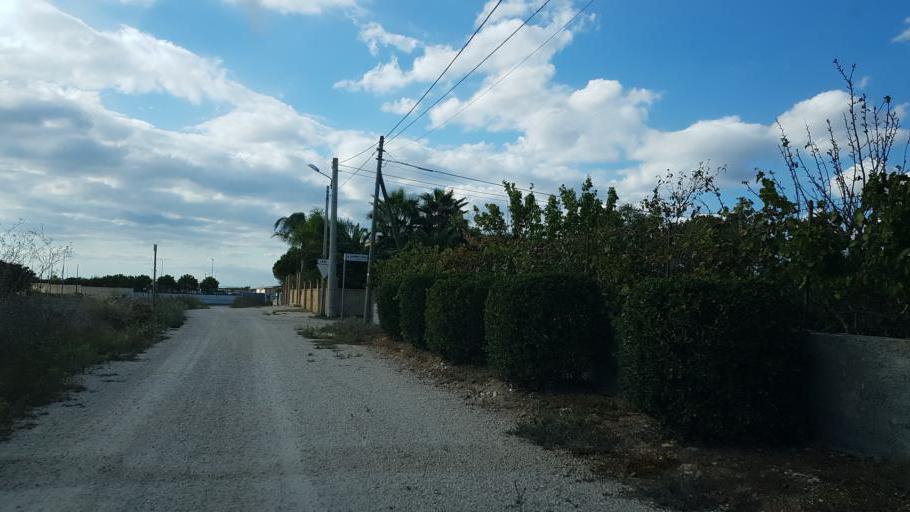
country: IT
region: Apulia
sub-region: Provincia di Lecce
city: Nardo
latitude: 40.1495
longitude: 18.0199
